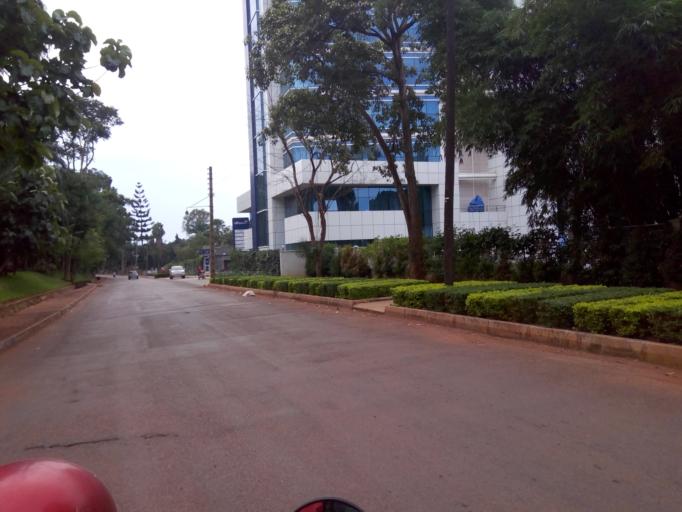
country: UG
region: Central Region
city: Kampala Central Division
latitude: 0.3256
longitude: 32.5824
